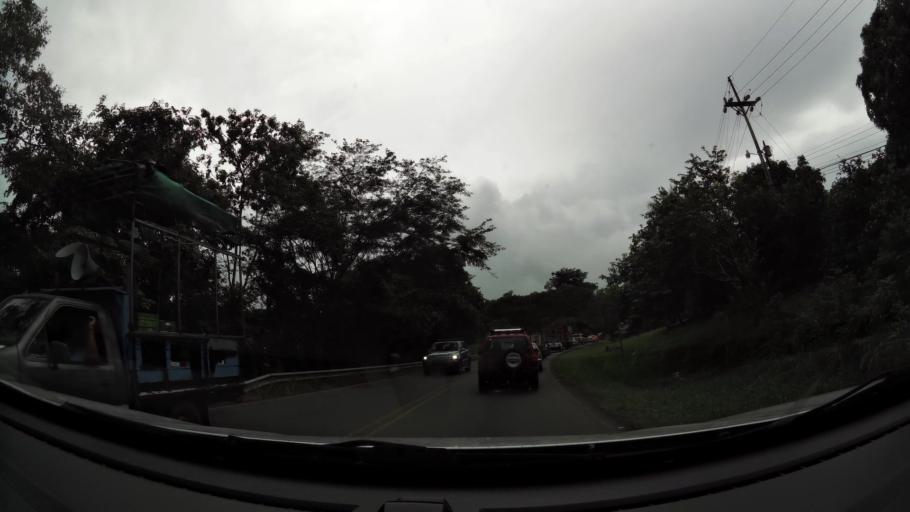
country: CR
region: Puntarenas
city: Esparza
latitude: 10.0015
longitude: -84.6756
